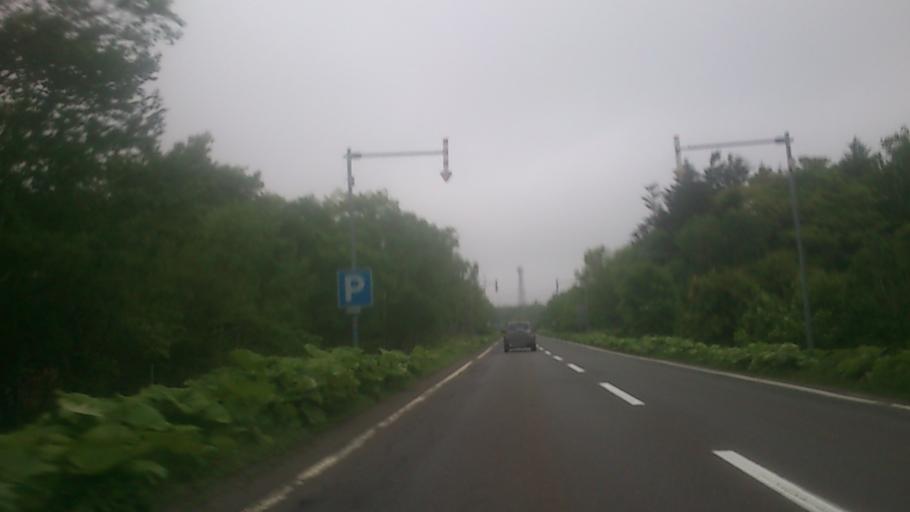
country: JP
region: Hokkaido
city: Kushiro
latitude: 42.9807
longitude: 144.5927
